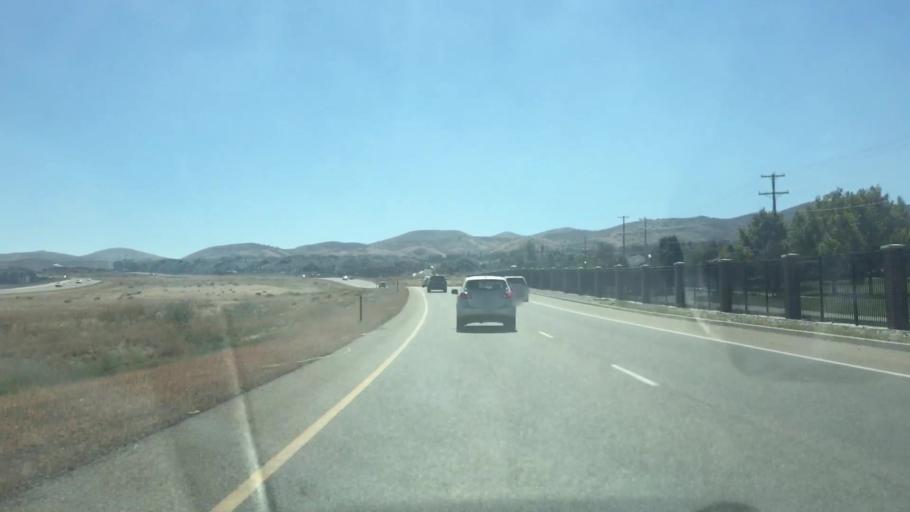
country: US
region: Utah
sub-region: Salt Lake County
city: Herriman
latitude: 40.4973
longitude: -112.0050
